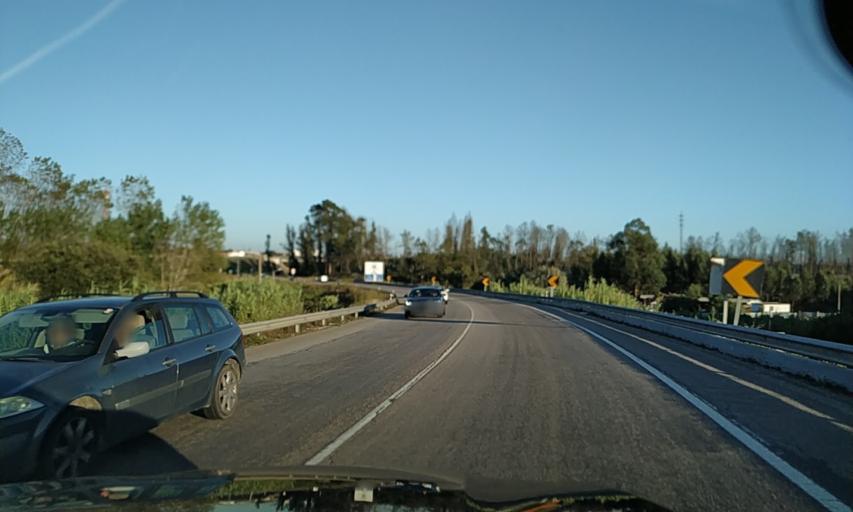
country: PT
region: Aveiro
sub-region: Aveiro
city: Oliveirinha
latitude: 40.5851
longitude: -8.6060
